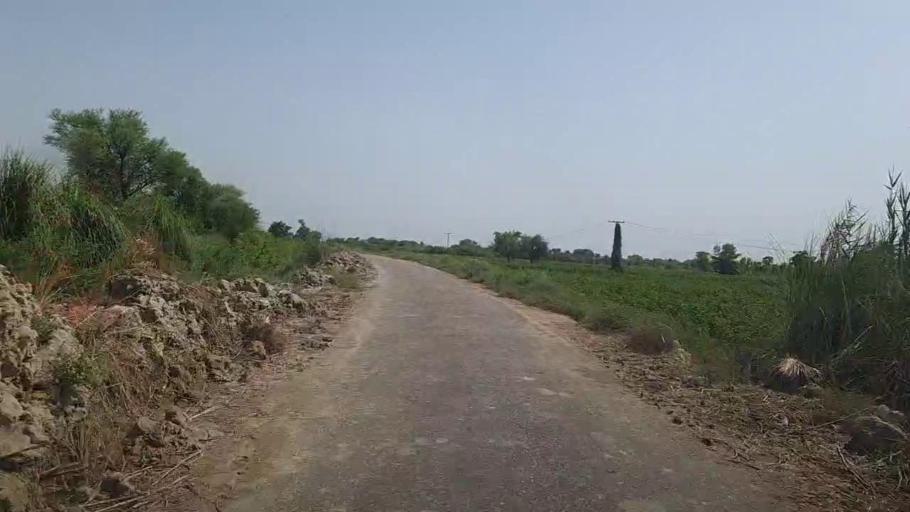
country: PK
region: Sindh
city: Pad Idan
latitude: 26.8243
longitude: 68.3280
